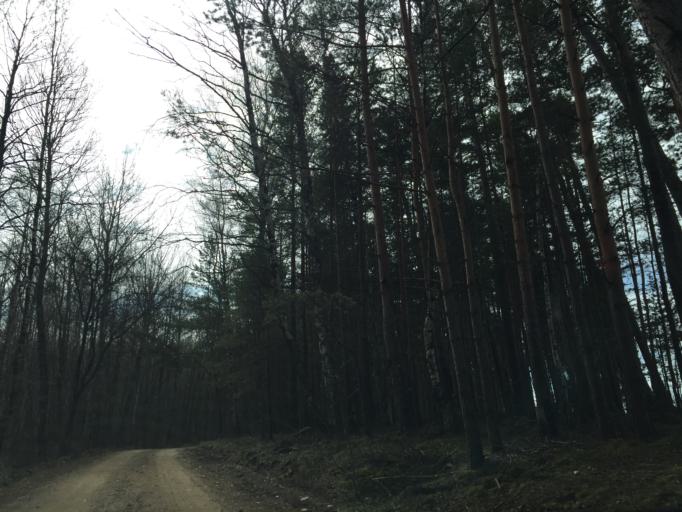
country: LV
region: Salacgrivas
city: Salacgriva
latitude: 57.5874
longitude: 24.3698
